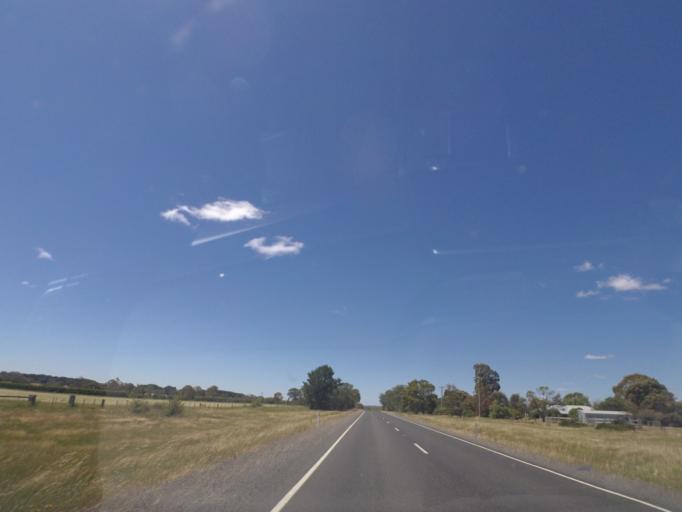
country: AU
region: Victoria
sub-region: Mount Alexander
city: Castlemaine
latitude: -37.2177
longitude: 144.3463
